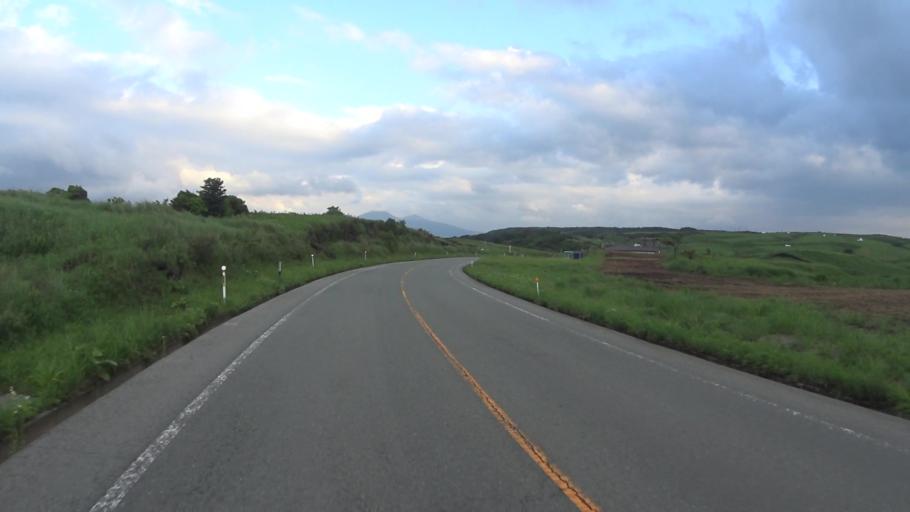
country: JP
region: Kumamoto
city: Aso
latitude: 32.9847
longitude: 131.0146
